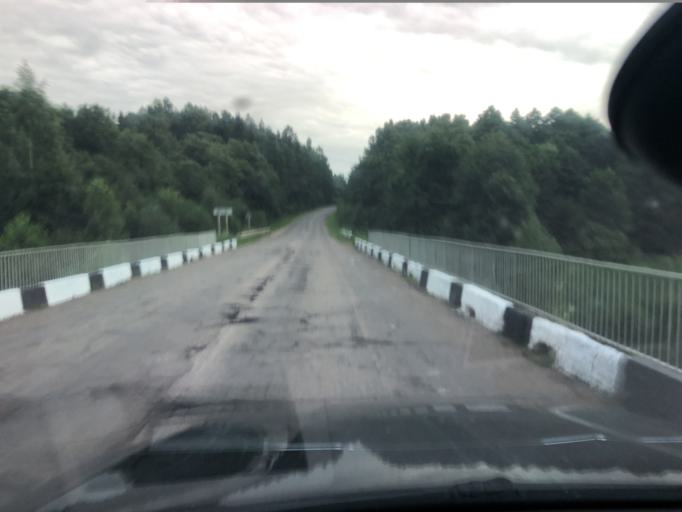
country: RU
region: Jaroslavl
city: Petrovsk
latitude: 56.9987
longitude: 39.0966
